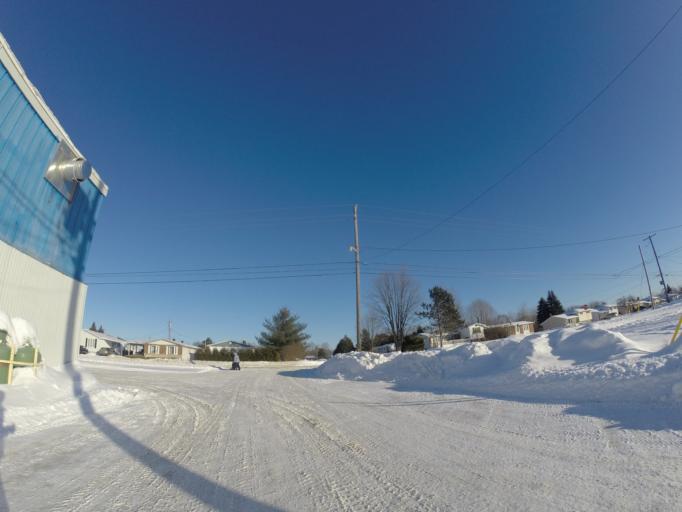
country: CA
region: Ontario
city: Rayside-Balfour
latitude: 46.5746
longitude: -81.1924
